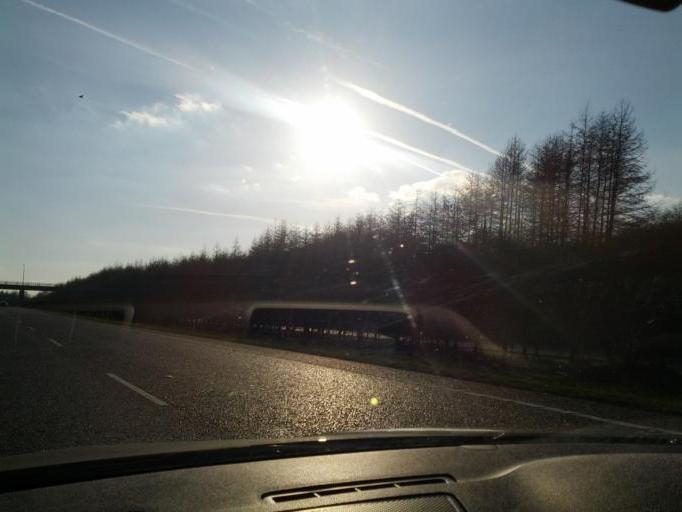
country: IE
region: Leinster
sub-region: Laois
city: Portlaoise
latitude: 53.0637
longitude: -7.2215
